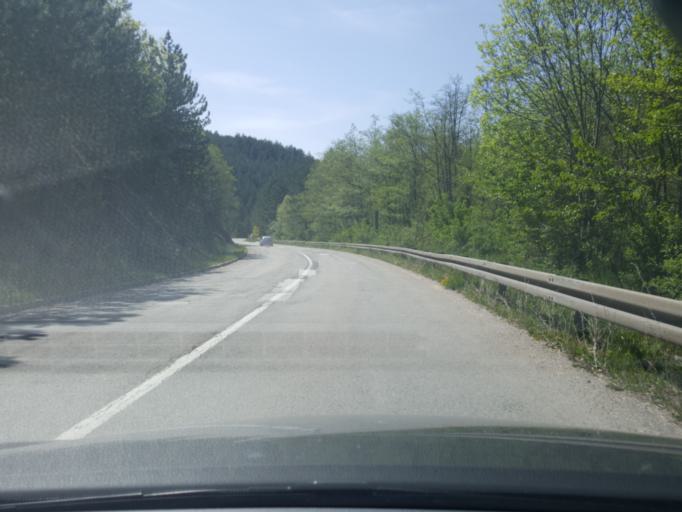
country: RS
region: Central Serbia
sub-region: Zlatiborski Okrug
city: Cajetina
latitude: 43.7861
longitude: 19.6702
